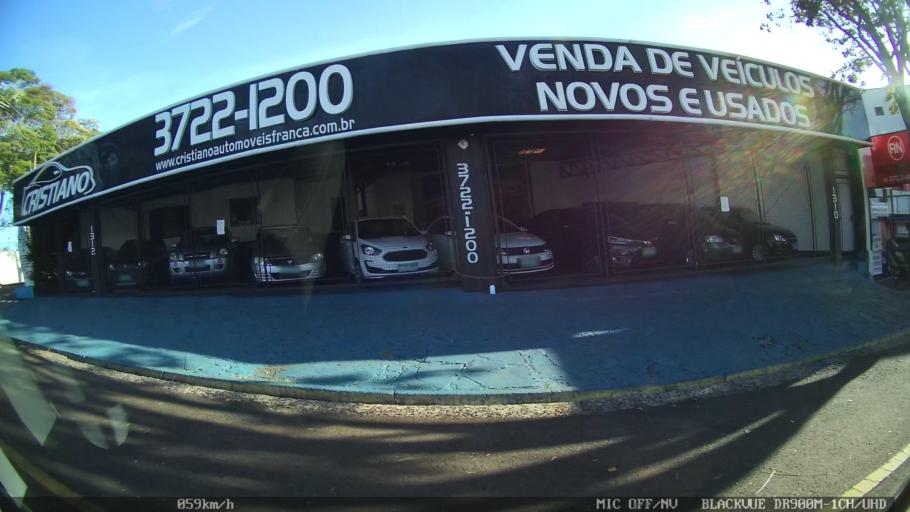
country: BR
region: Sao Paulo
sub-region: Franca
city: Franca
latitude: -20.5303
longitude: -47.3994
